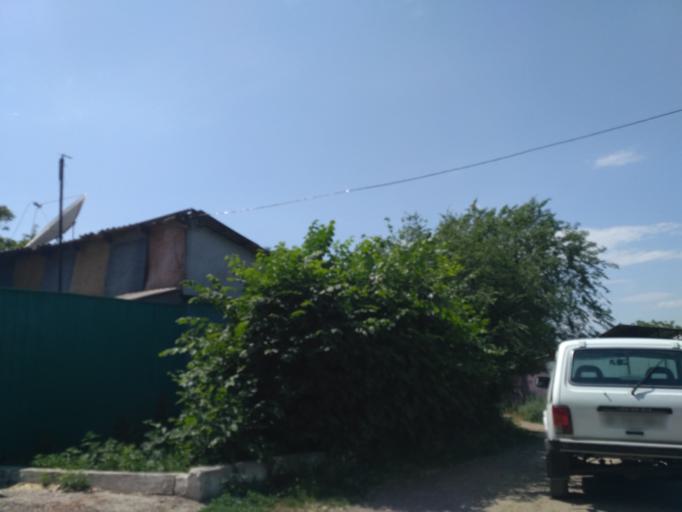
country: KZ
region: Almaty Oblysy
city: Burunday
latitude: 43.1897
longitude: 76.6187
